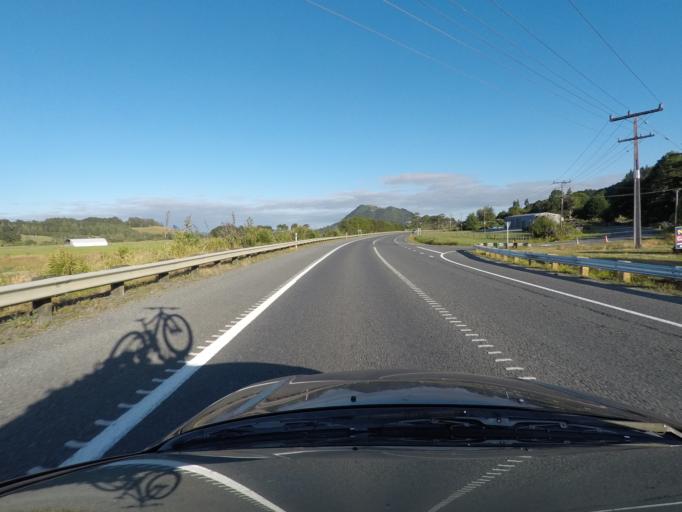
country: NZ
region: Northland
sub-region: Whangarei
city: Whangarei
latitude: -35.6241
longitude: 174.2919
